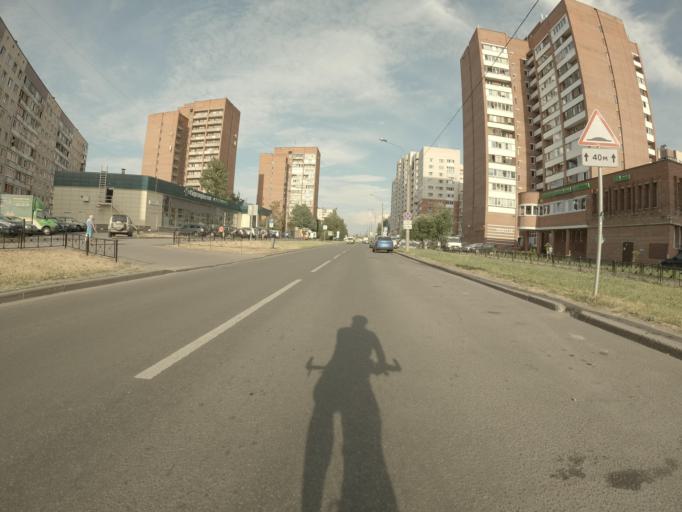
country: RU
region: St.-Petersburg
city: Krasnogvargeisky
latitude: 59.9402
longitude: 30.4931
